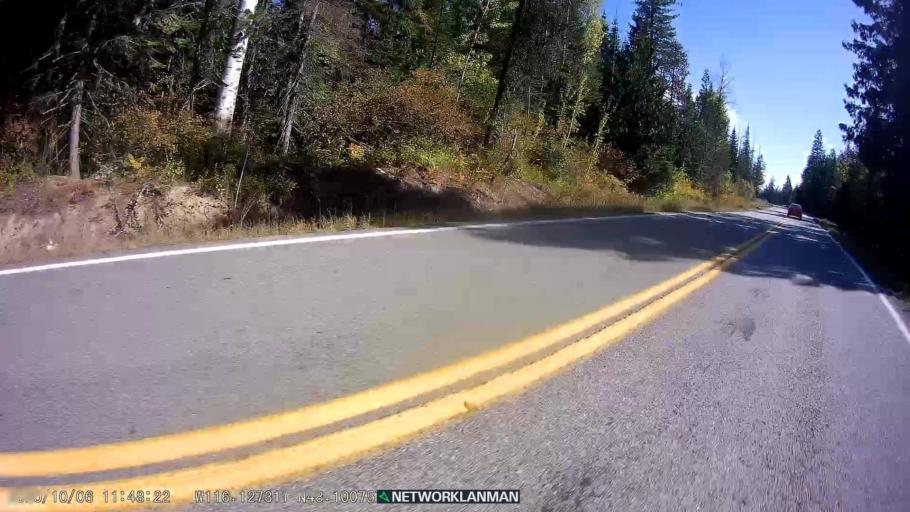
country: US
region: Idaho
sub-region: Bonner County
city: Ponderay
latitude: 48.1008
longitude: -116.1272
